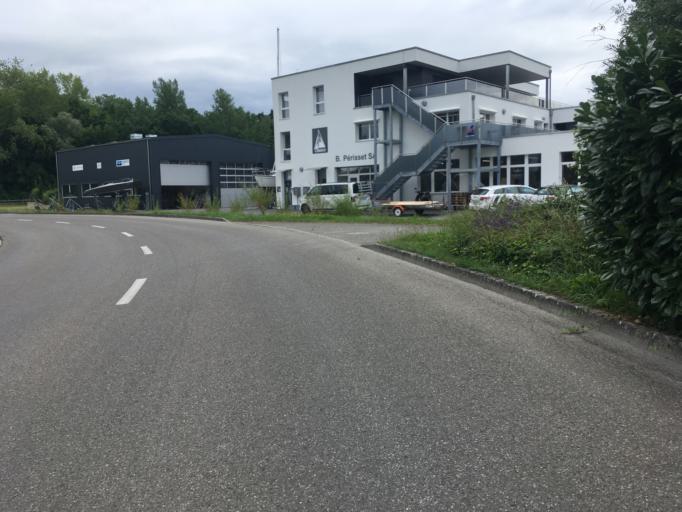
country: CH
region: Fribourg
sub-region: Broye District
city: Estavayer-le-Lac
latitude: 46.8474
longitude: 6.8379
